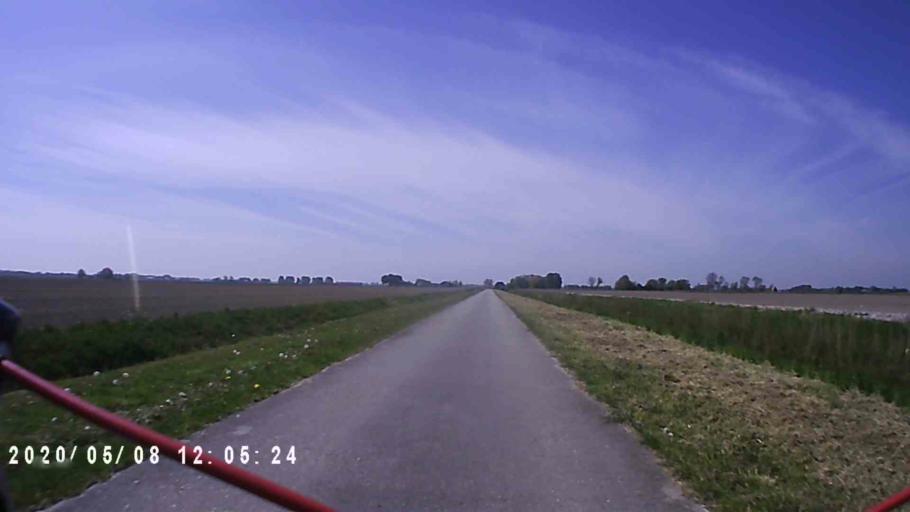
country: NL
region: Groningen
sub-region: Gemeente Bedum
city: Bedum
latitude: 53.3006
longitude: 6.6947
